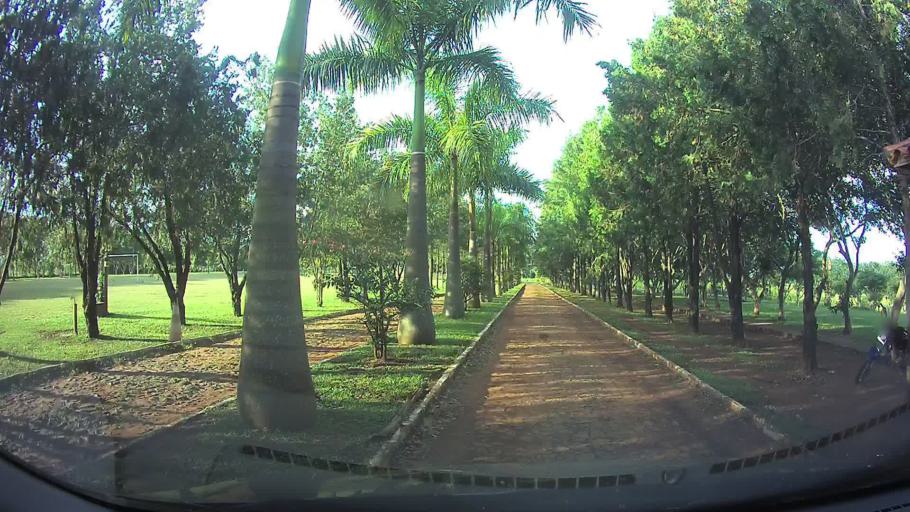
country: PY
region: Paraguari
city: Ybycui
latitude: -25.9976
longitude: -57.0507
